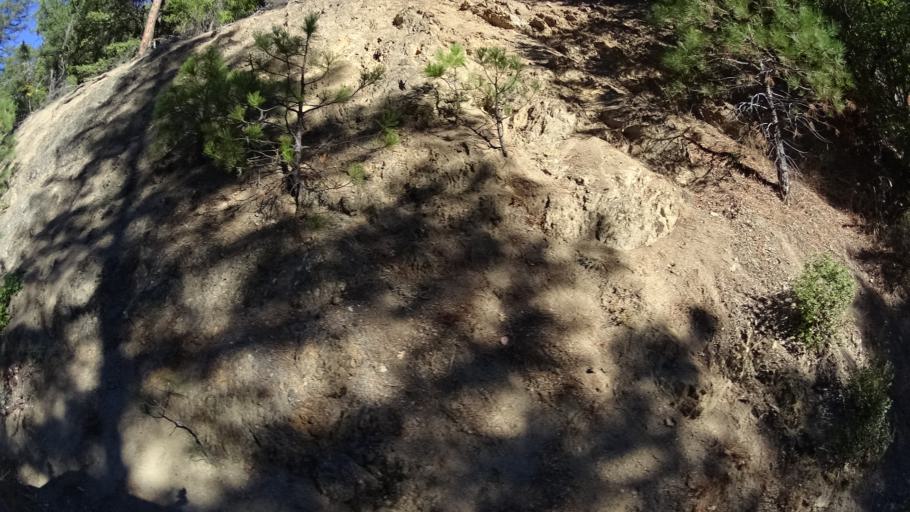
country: US
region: California
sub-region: Trinity County
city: Weaverville
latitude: 41.2125
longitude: -123.0323
